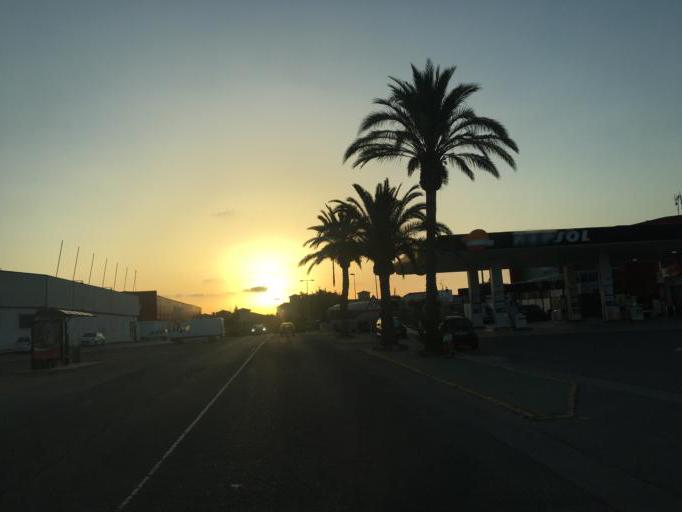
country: ES
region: Murcia
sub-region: Murcia
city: La Manga del Mar Menor
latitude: 37.6281
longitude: -0.7095
